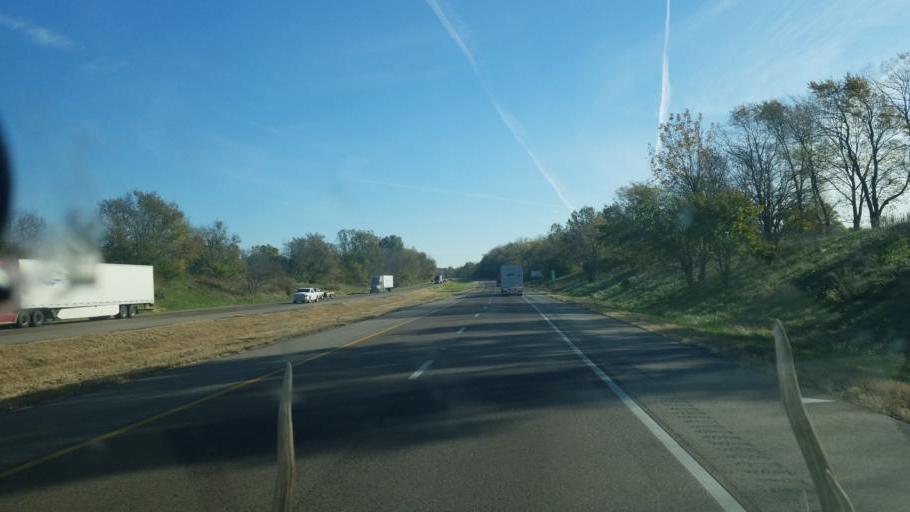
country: US
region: Illinois
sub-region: Madison County
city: Troy
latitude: 38.7565
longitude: -89.8473
